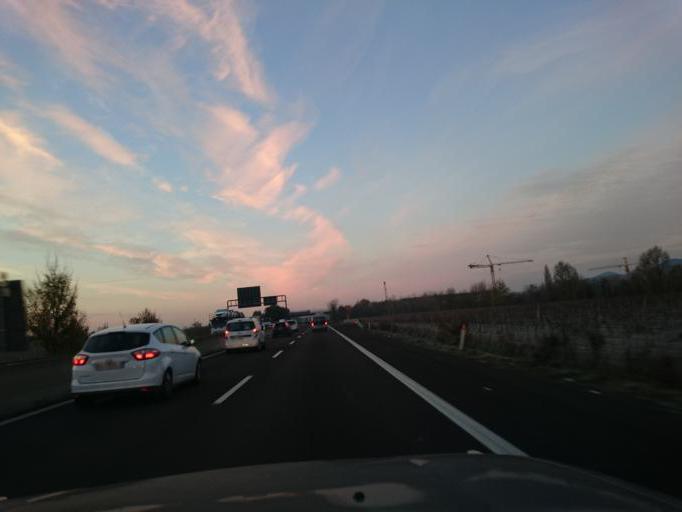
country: IT
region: Veneto
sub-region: Provincia di Padova
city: Terradura
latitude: 45.3286
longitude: 11.8354
